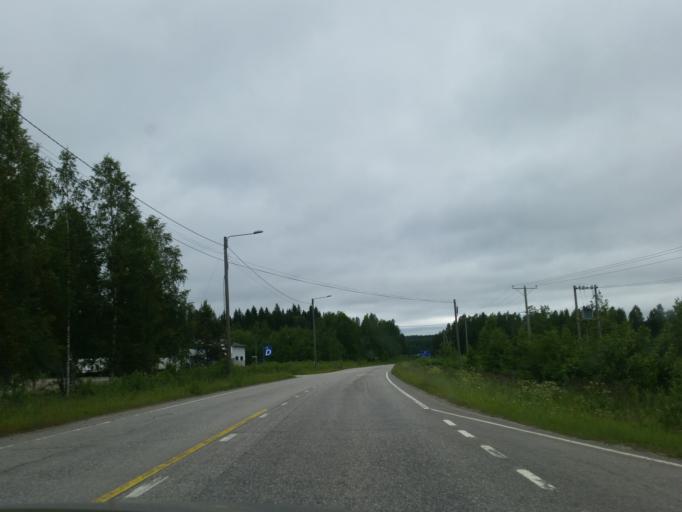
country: FI
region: Northern Savo
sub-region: Koillis-Savo
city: Kaavi
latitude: 62.9735
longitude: 28.5021
